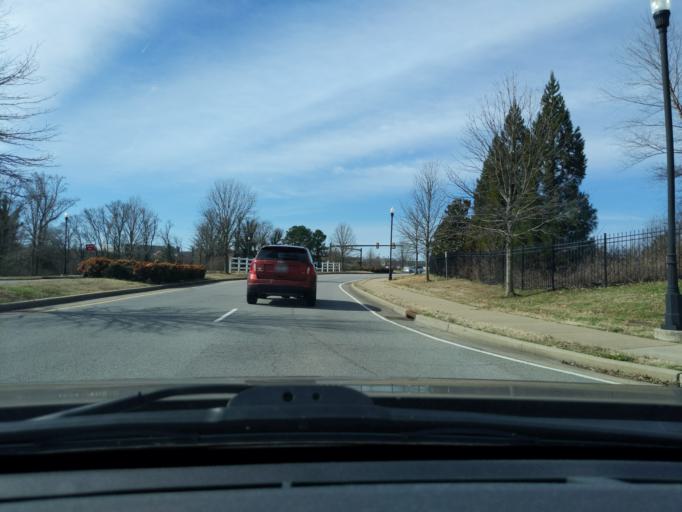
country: US
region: Tennessee
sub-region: Wilson County
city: Mount Juliet
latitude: 36.1781
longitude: -86.5140
